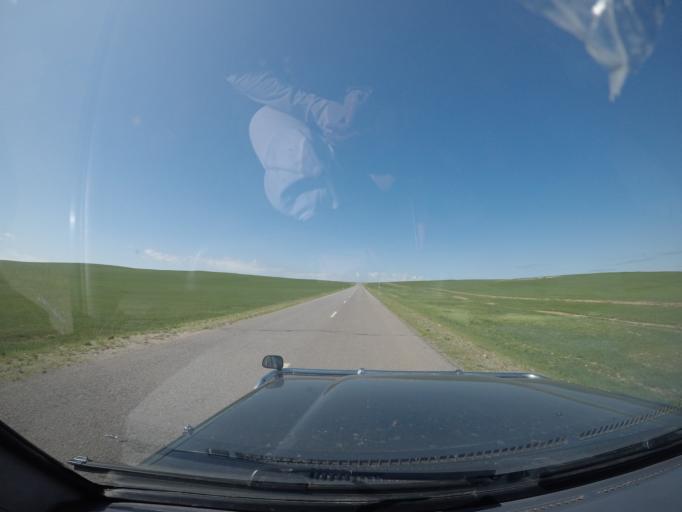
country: MN
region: Suhbaatar
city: Bayasgalant
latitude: 47.3534
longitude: 111.6554
